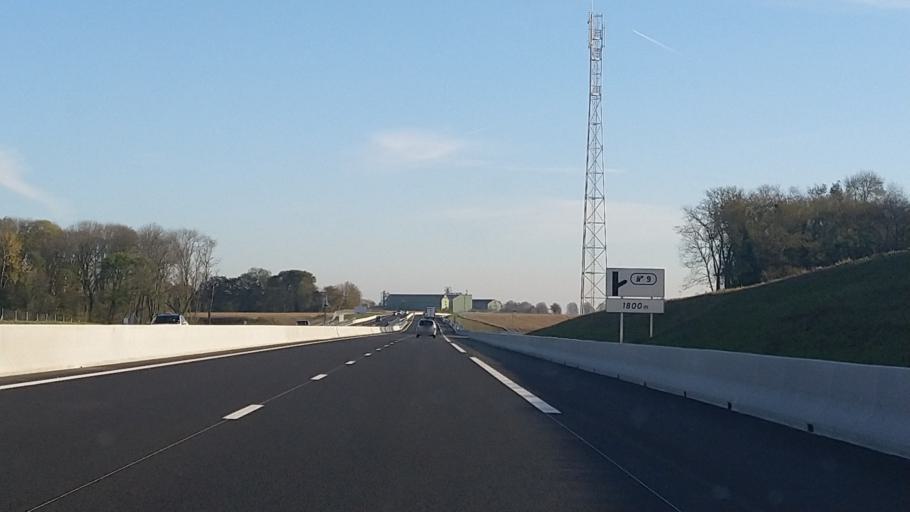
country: FR
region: Ile-de-France
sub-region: Departement du Val-d'Oise
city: Maffliers
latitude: 49.0850
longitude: 2.3190
